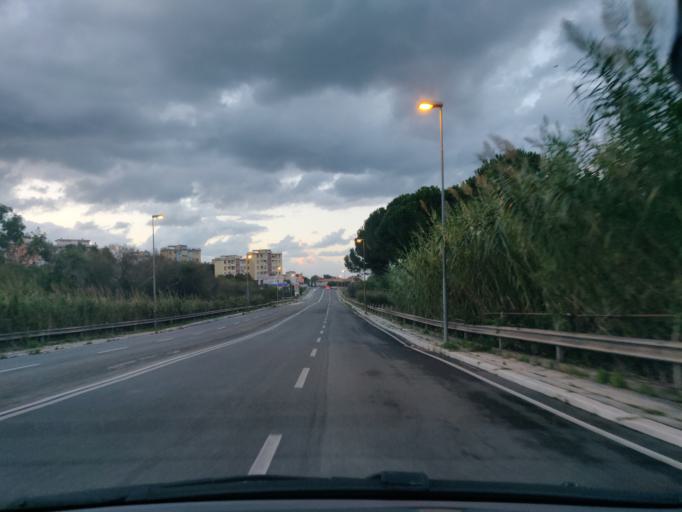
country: IT
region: Latium
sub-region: Citta metropolitana di Roma Capitale
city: Civitavecchia
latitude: 42.0841
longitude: 11.8087
